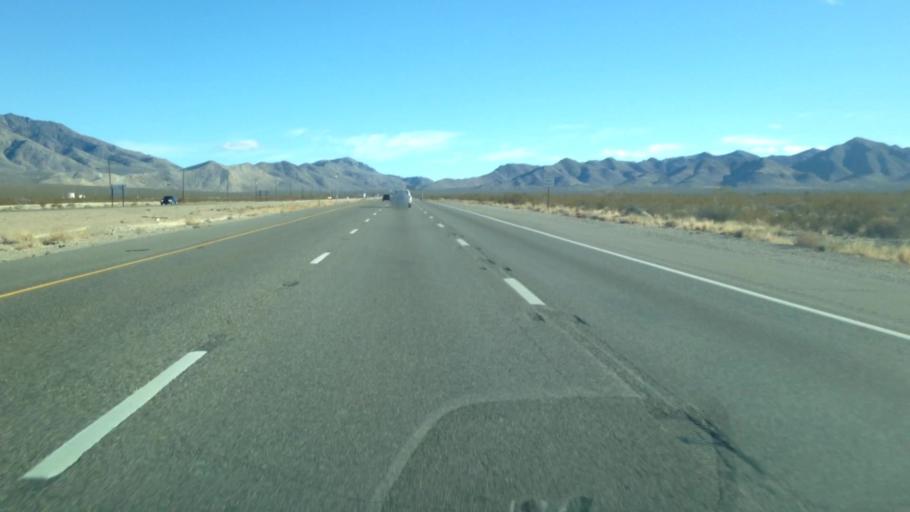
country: US
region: Nevada
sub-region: Clark County
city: Sandy Valley
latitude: 35.4461
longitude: -115.6679
